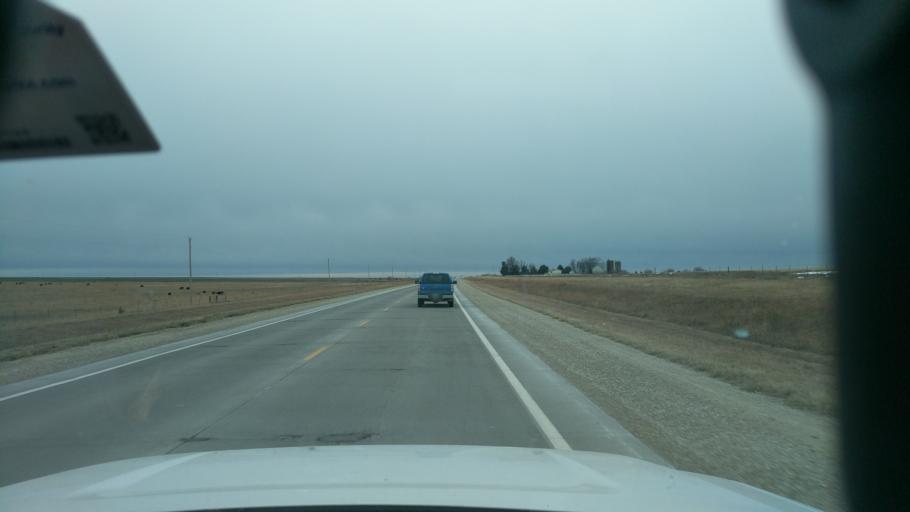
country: US
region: Kansas
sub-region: Dickinson County
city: Herington
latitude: 38.6019
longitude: -96.9484
